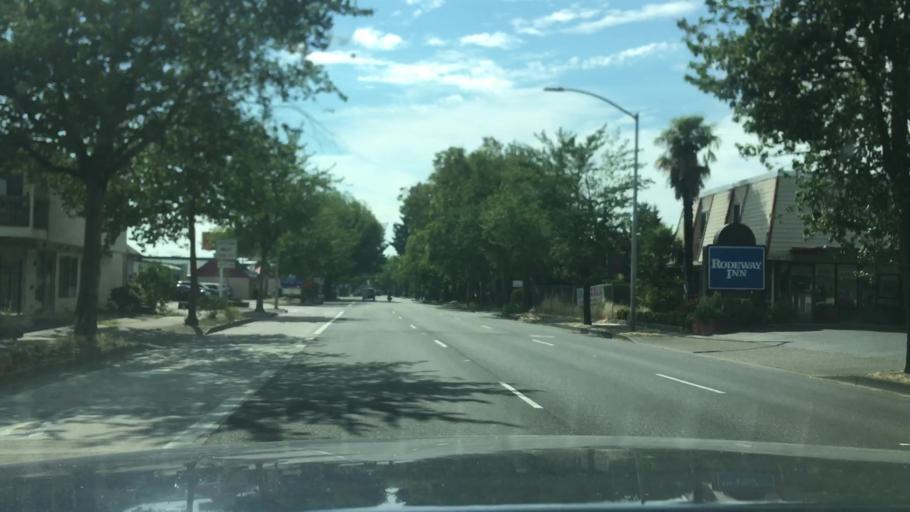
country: US
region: Oregon
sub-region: Lane County
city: Eugene
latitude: 44.0533
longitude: -123.1087
